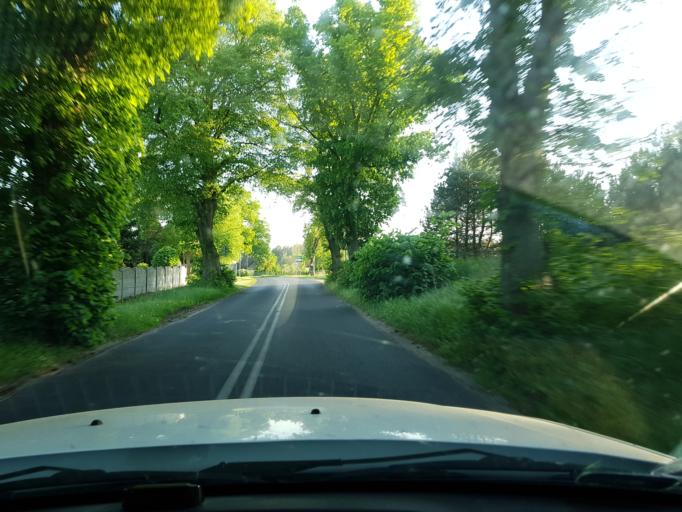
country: PL
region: West Pomeranian Voivodeship
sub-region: Powiat stargardzki
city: Kobylanka
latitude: 53.4320
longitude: 14.9021
